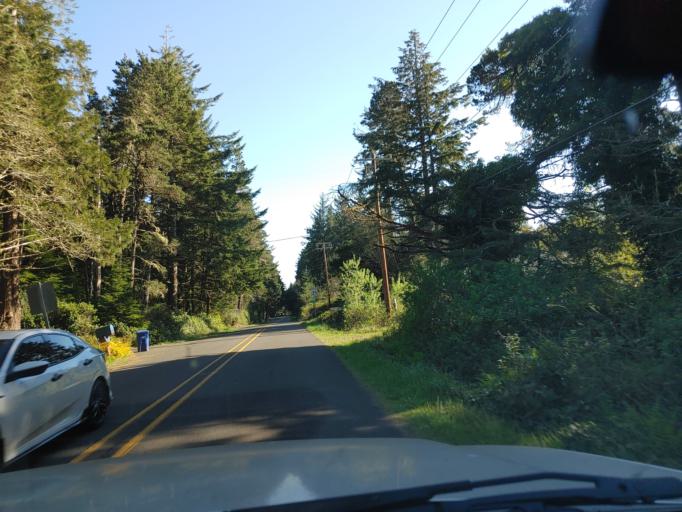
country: US
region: Oregon
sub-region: Lincoln County
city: Depoe Bay
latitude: 44.7457
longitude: -124.0559
